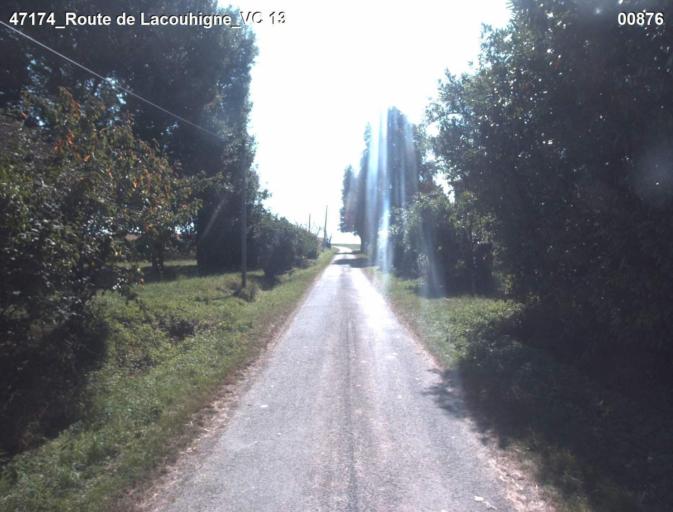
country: FR
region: Midi-Pyrenees
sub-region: Departement du Gers
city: Condom
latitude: 44.0213
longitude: 0.3827
